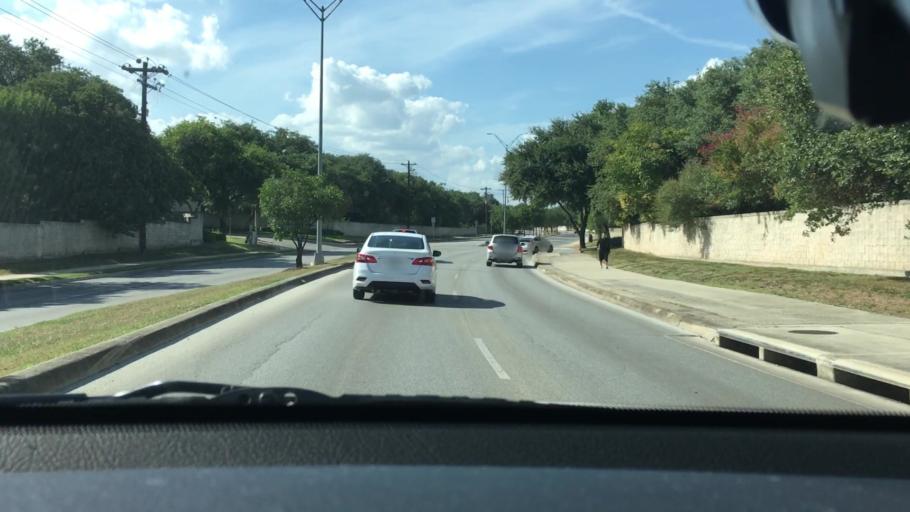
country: US
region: Texas
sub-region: Bexar County
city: Selma
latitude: 29.5779
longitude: -98.2804
